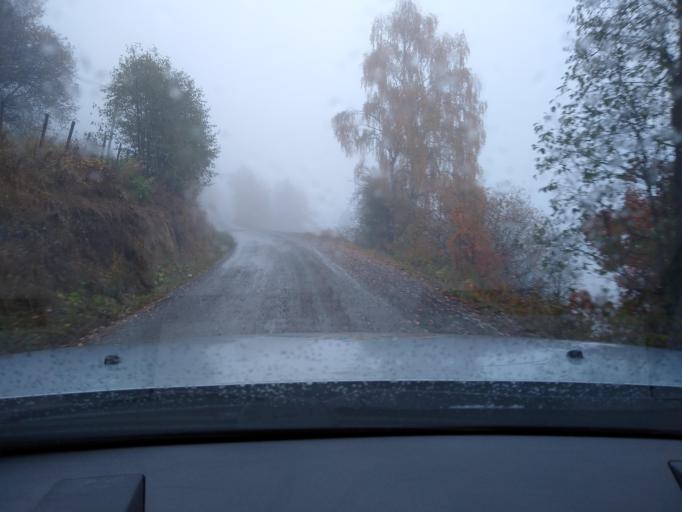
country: NO
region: Oppland
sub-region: Ringebu
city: Ringebu
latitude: 61.5282
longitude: 10.1576
